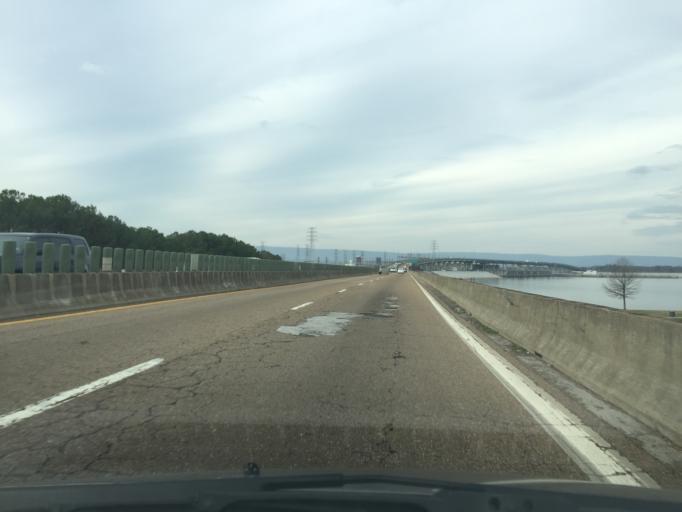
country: US
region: Tennessee
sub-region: Hamilton County
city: East Chattanooga
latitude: 35.0952
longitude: -85.2255
